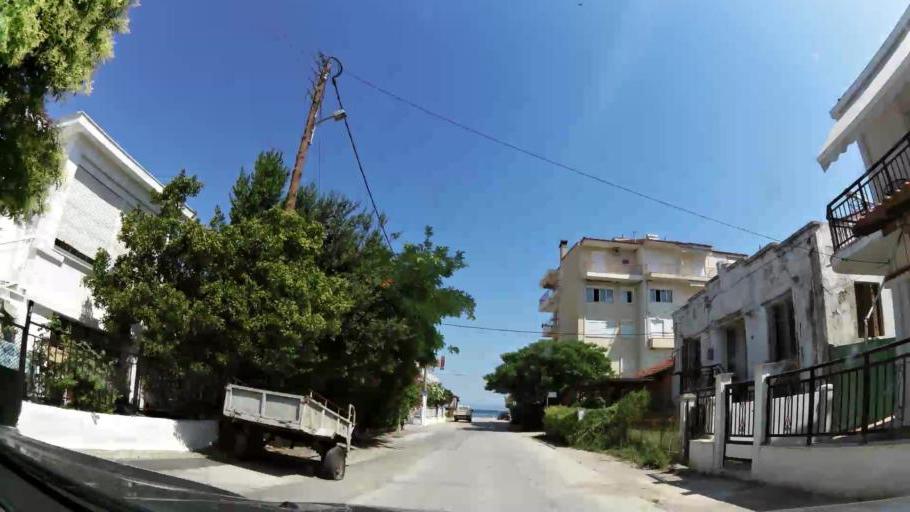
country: GR
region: Central Macedonia
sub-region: Nomos Thessalonikis
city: Agia Triada
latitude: 40.5001
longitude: 22.8789
